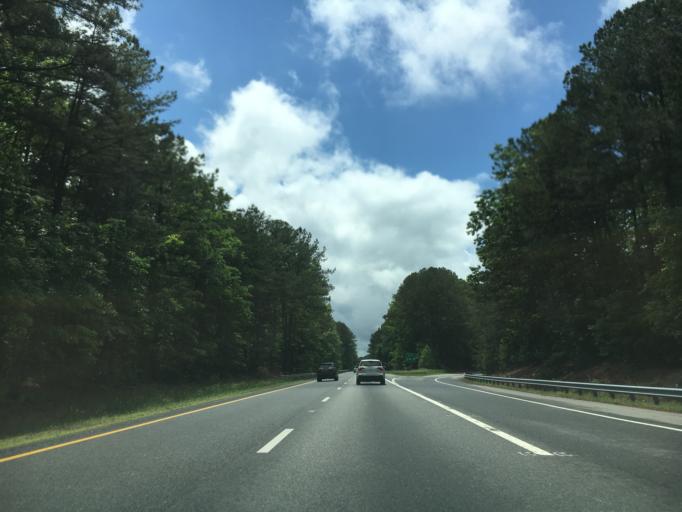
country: US
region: Virginia
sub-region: Brunswick County
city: Lawrenceville
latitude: 36.8245
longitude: -77.9556
